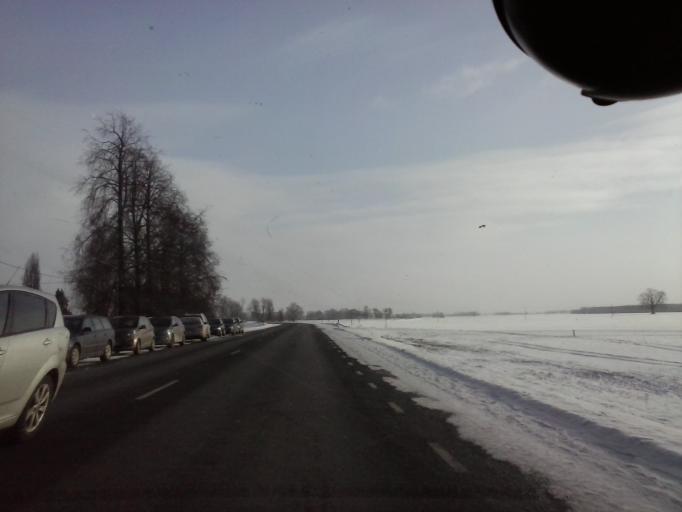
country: EE
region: Tartu
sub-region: Puhja vald
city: Puhja
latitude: 58.3352
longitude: 26.1845
